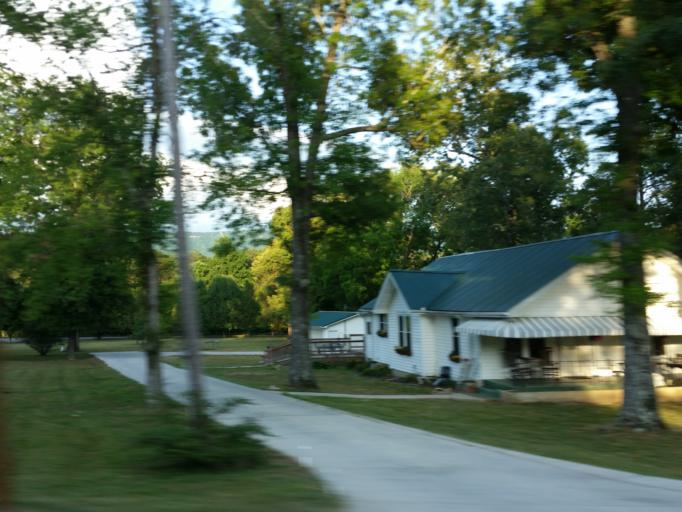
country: US
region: Georgia
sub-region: Dade County
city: Trenton
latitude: 34.8899
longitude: -85.4985
